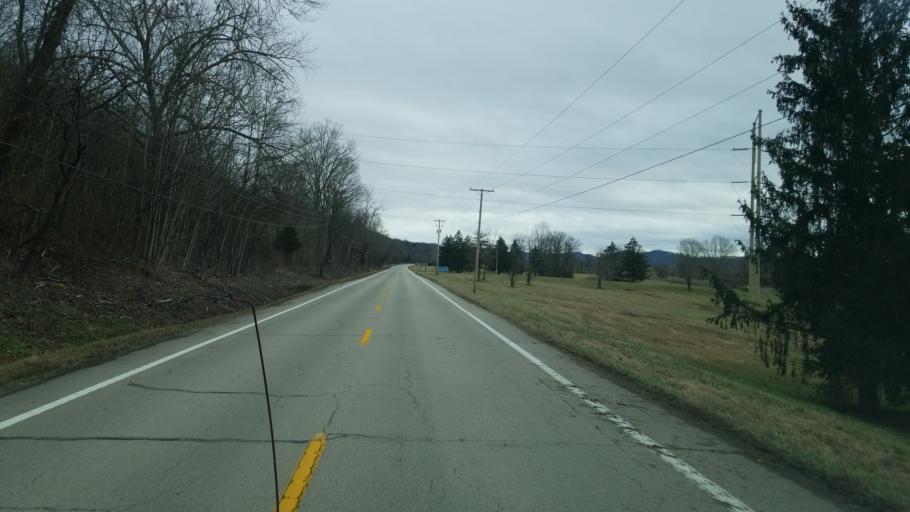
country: US
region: Ohio
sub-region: Adams County
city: West Union
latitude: 38.6958
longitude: -83.4773
